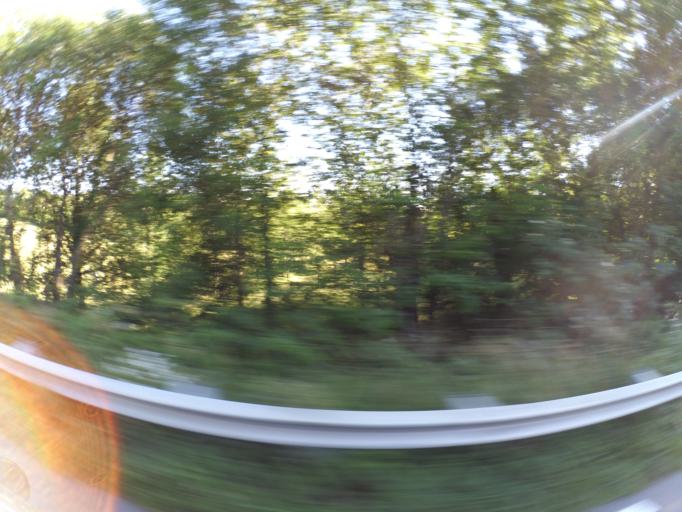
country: FR
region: Pays de la Loire
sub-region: Departement de la Vendee
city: Saint-Michel-Mont-Mercure
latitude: 46.8400
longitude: -0.9112
